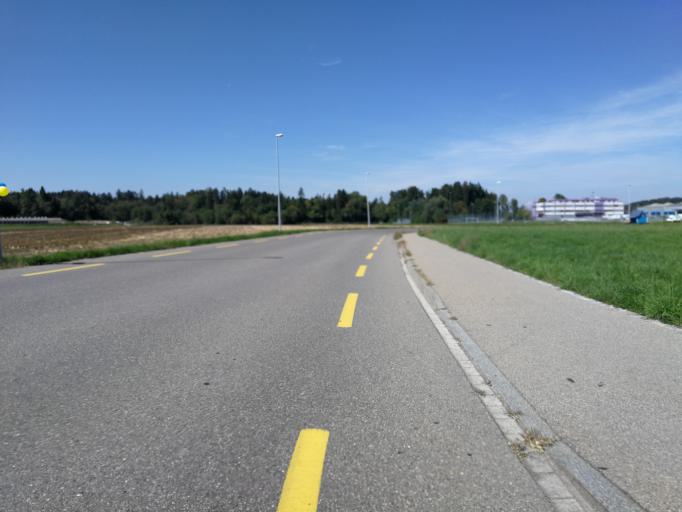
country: CH
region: Zurich
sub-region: Bezirk Pfaeffikon
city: Pfaeffikon / Pfaeffikon (Dorfkern)
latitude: 47.3675
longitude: 8.7693
